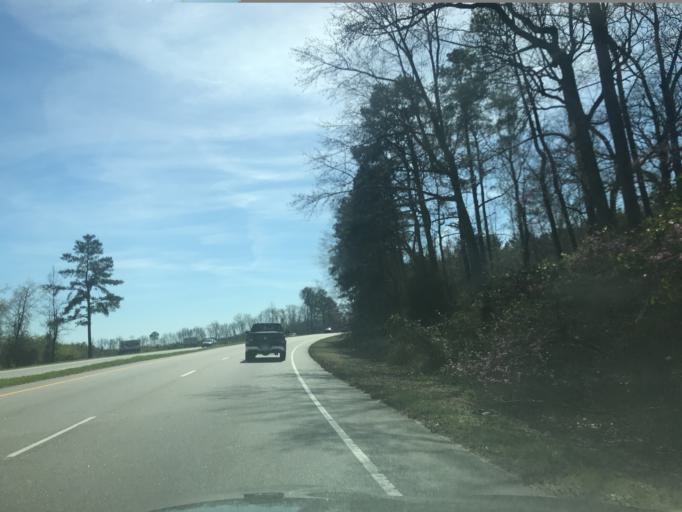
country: US
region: North Carolina
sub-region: Wake County
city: Garner
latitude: 35.6781
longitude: -78.6870
